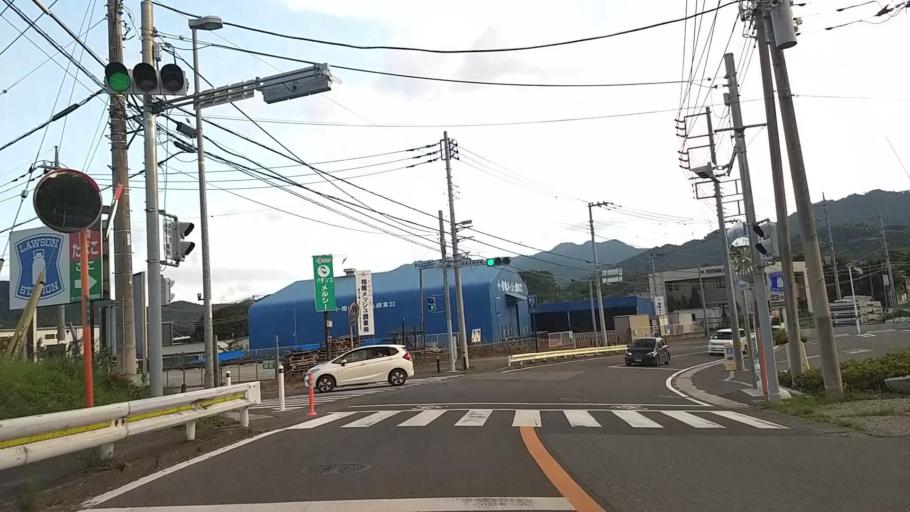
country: JP
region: Tokyo
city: Hachioji
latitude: 35.5698
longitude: 139.2631
